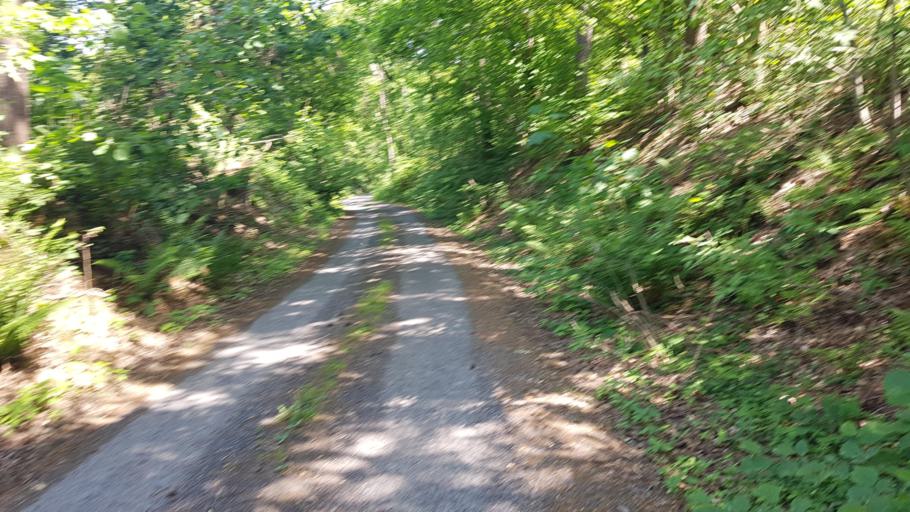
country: DE
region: Brandenburg
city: Grosskmehlen
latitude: 51.3638
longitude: 13.7074
